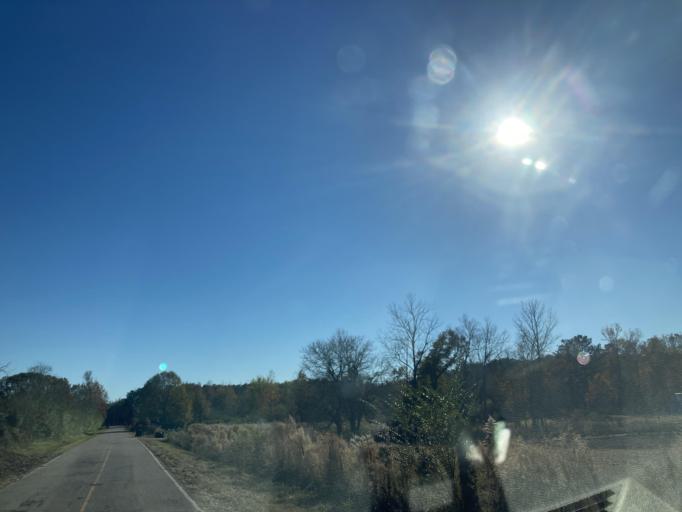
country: US
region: Mississippi
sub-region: Lamar County
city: Sumrall
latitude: 31.3853
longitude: -89.6075
